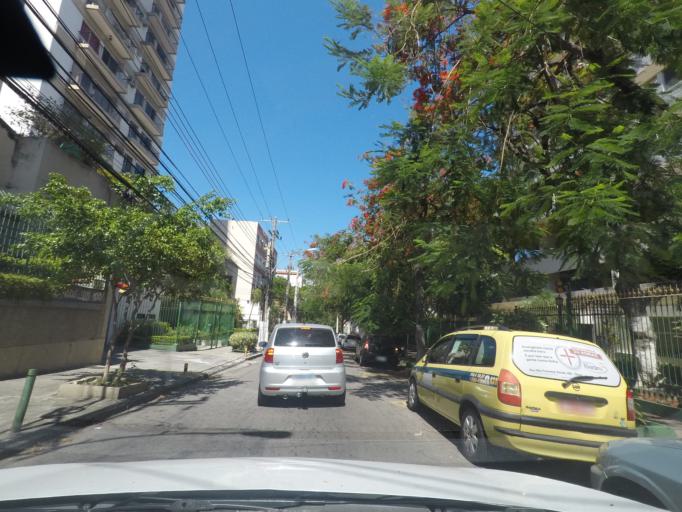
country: BR
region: Rio de Janeiro
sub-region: Rio De Janeiro
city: Rio de Janeiro
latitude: -22.9135
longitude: -43.2503
